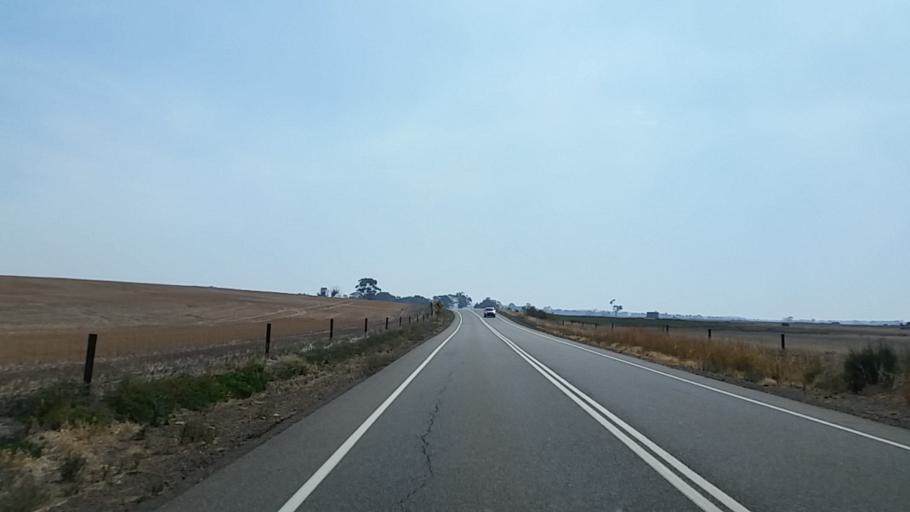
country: AU
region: South Australia
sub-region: Light
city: Kapunda
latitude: -34.2556
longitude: 138.7541
